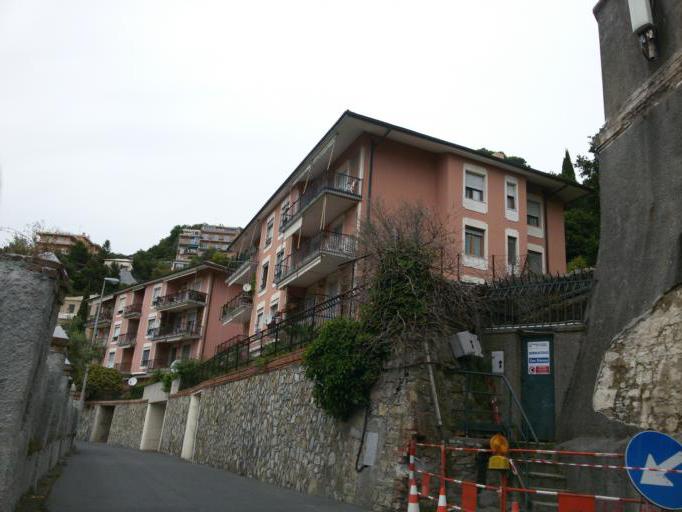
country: IT
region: Liguria
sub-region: Provincia di Genova
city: Genoa
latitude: 44.4240
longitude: 8.9344
